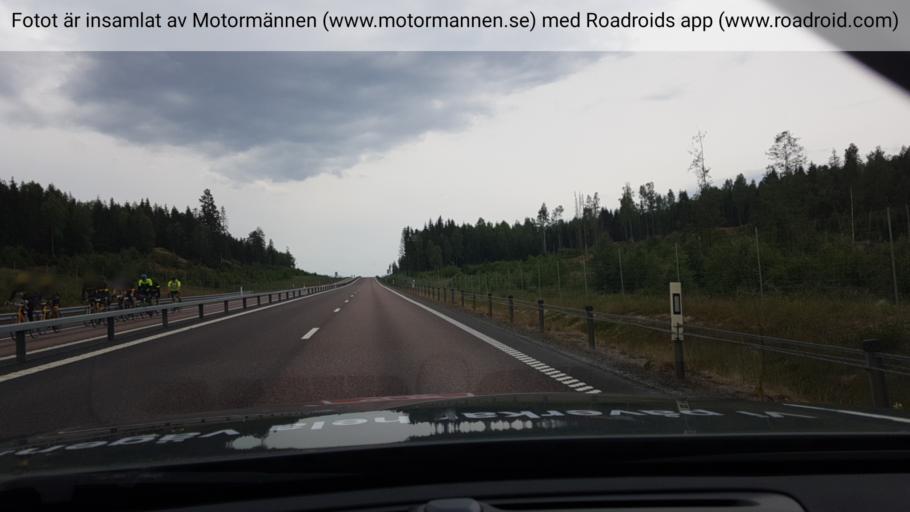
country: SE
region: OErebro
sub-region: Askersunds Kommun
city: Askersund
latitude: 58.8441
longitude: 14.9066
